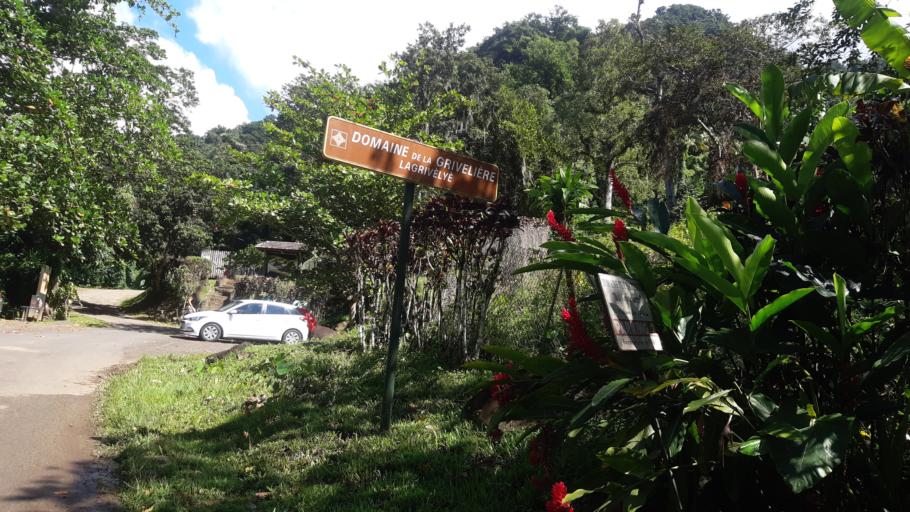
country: GP
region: Guadeloupe
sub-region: Guadeloupe
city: Vieux-Habitants
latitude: 16.0729
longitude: -61.7285
